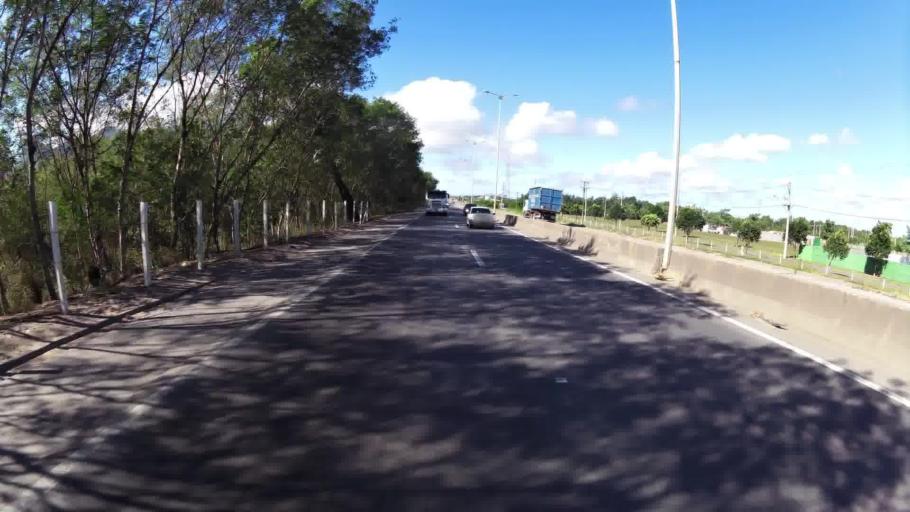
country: BR
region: Espirito Santo
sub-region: Serra
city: Serra
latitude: -20.2149
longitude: -40.3238
